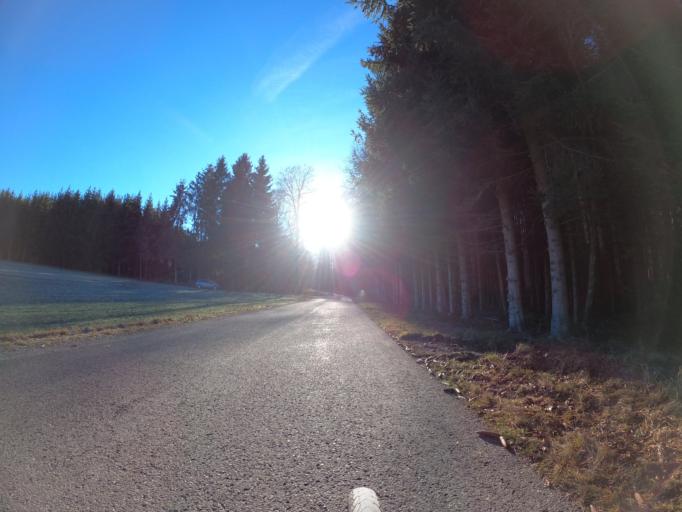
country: DE
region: Baden-Wuerttemberg
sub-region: Tuebingen Region
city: Sankt Johann
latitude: 48.4392
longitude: 9.2971
